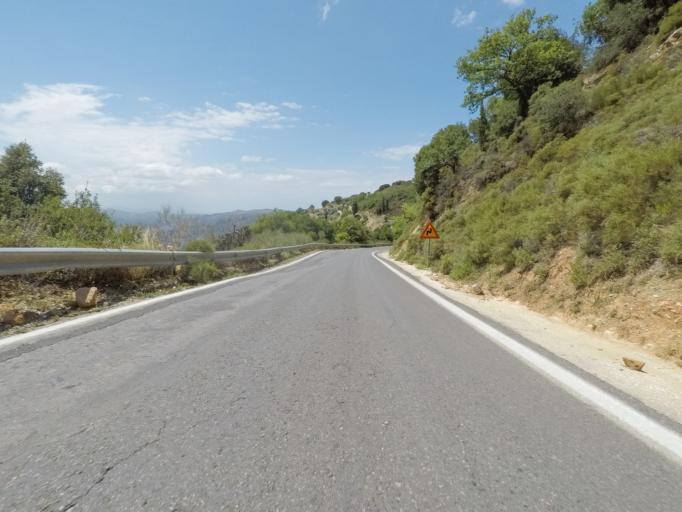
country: GR
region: Crete
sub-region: Nomos Irakleiou
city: Mokhos
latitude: 35.2254
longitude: 25.4627
